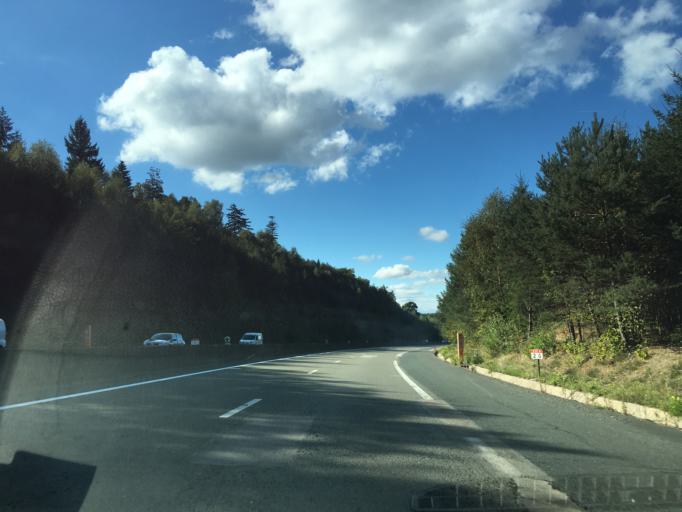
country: FR
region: Lorraine
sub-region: Departement des Vosges
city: Etival-Clairefontaine
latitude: 48.3964
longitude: 6.8368
